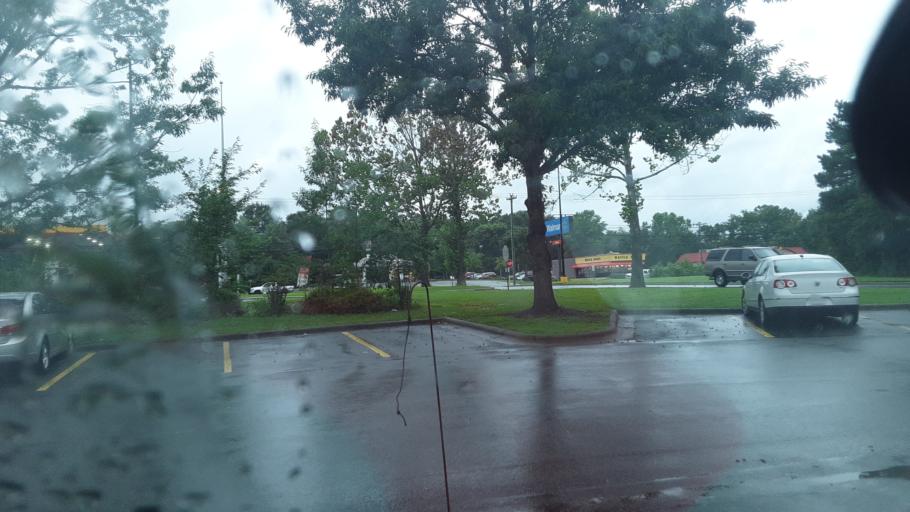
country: US
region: North Carolina
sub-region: Surry County
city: Toast
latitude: 36.4737
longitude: -80.6195
